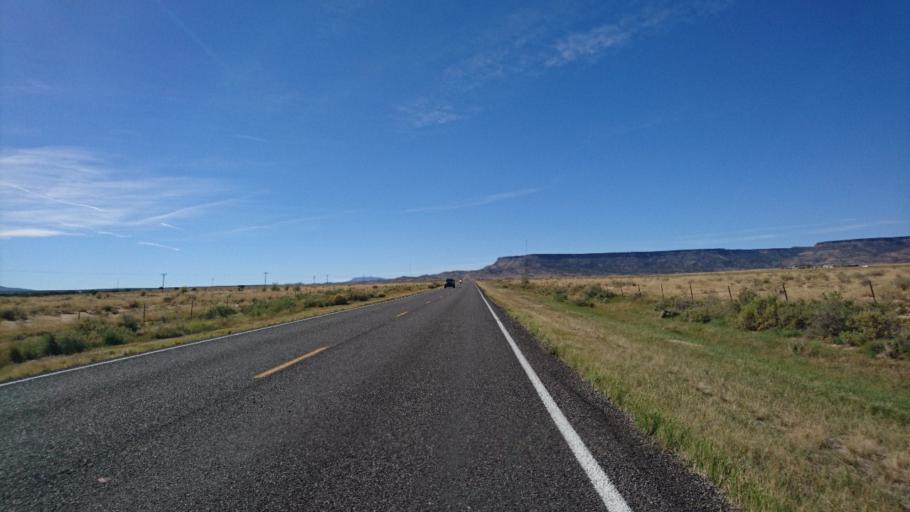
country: US
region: New Mexico
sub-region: Cibola County
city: Skyline-Ganipa
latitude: 35.0825
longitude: -107.6173
